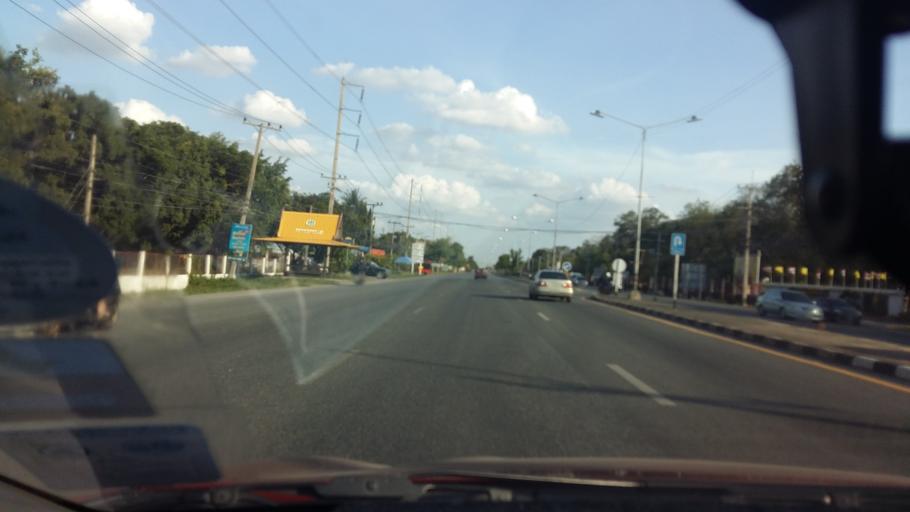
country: TH
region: Lop Buri
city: Lop Buri
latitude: 14.8452
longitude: 100.6431
